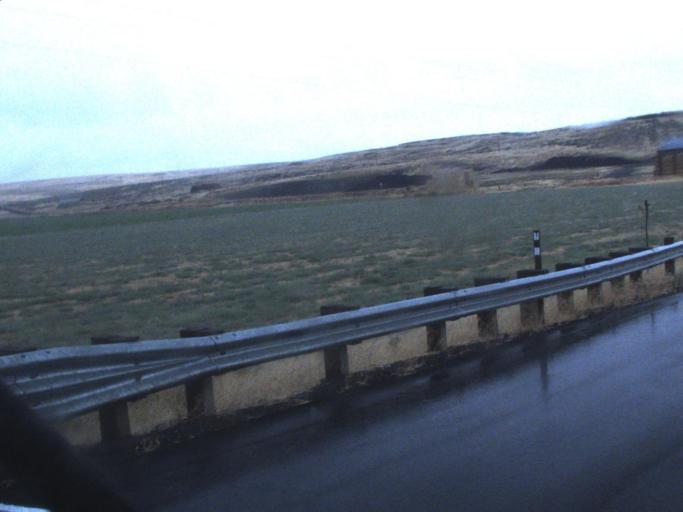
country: US
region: Washington
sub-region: Lincoln County
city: Davenport
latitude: 47.3607
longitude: -118.1085
